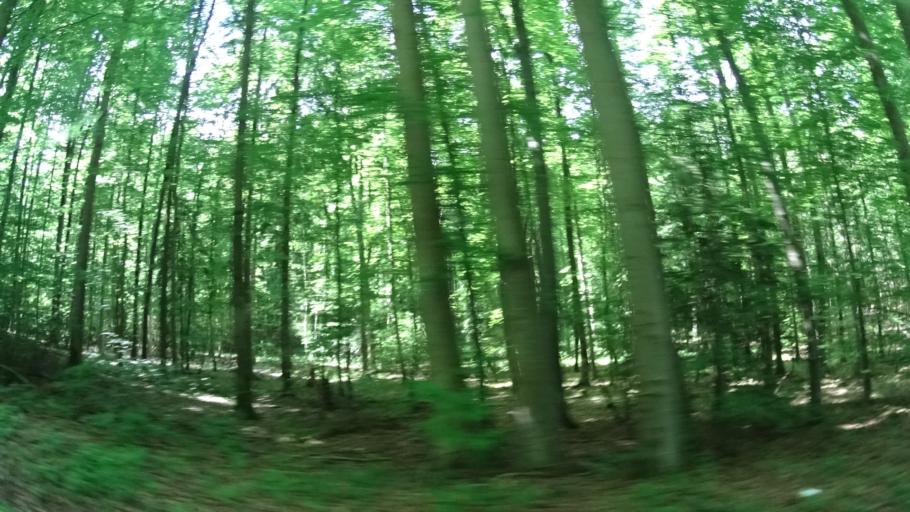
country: DE
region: Bavaria
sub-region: Regierungsbezirk Unterfranken
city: Zellingen
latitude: 49.8782
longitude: 9.7669
